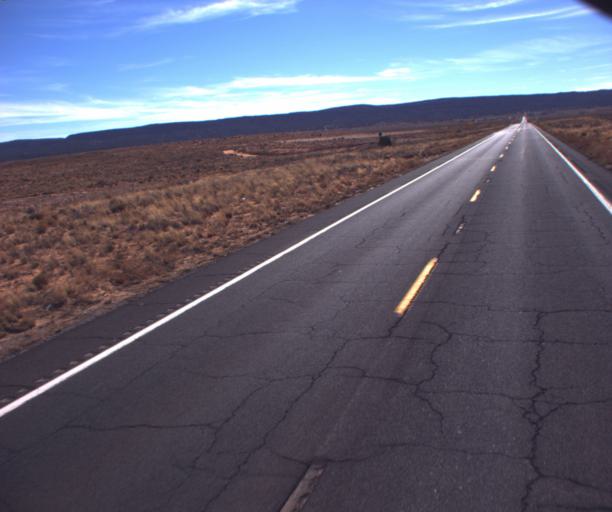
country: US
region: Arizona
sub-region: Coconino County
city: Kaibito
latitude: 36.4822
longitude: -110.7039
